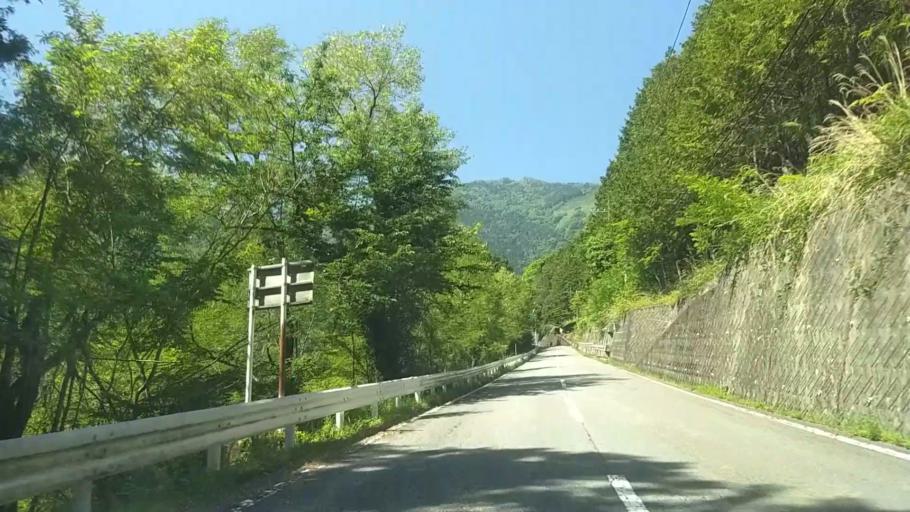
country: JP
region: Yamanashi
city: Ryuo
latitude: 35.5082
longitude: 138.4022
